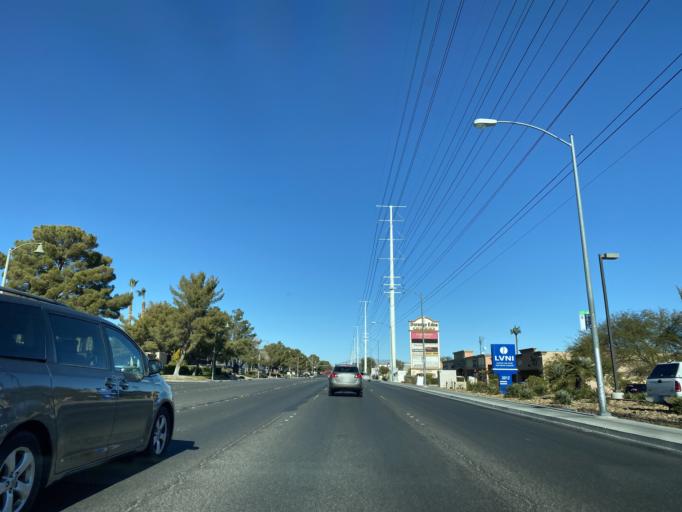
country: US
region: Nevada
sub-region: Clark County
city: Spring Valley
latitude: 36.1341
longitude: -115.2789
